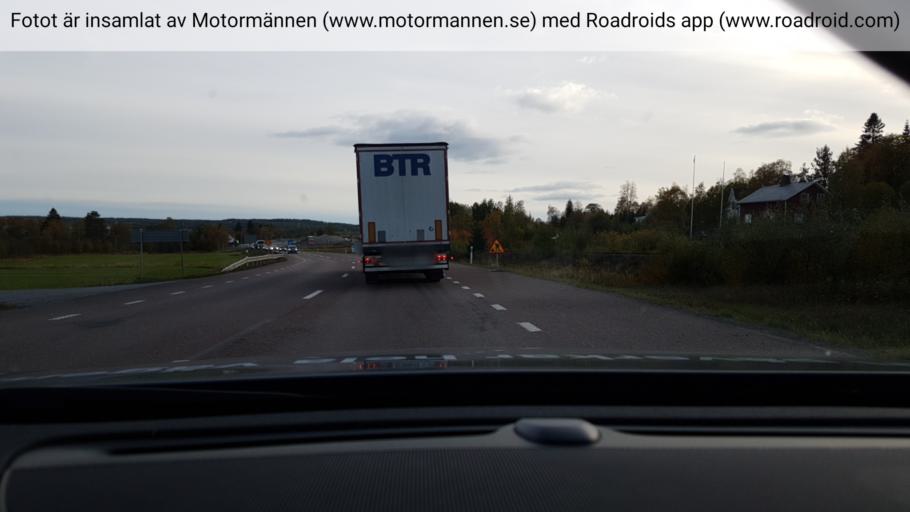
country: SE
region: Vaesternorrland
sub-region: Haernoesands Kommun
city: Haernoesand
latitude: 62.6859
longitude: 17.8467
